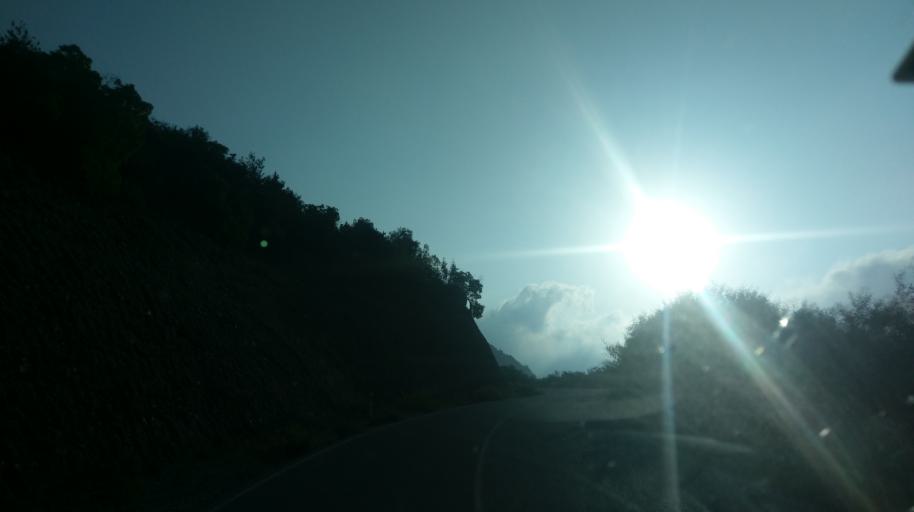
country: CY
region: Ammochostos
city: Trikomo
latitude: 35.4021
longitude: 33.9045
